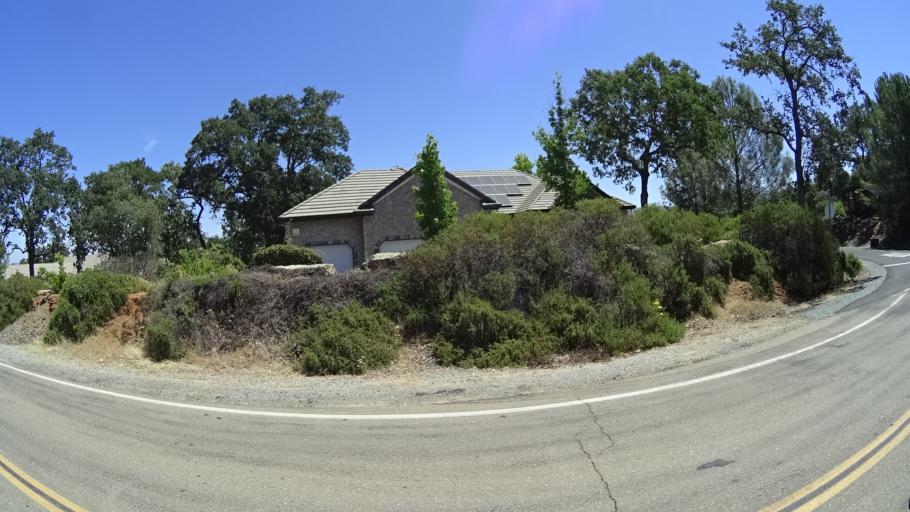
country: US
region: California
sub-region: Calaveras County
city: Valley Springs
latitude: 38.1642
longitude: -120.8388
